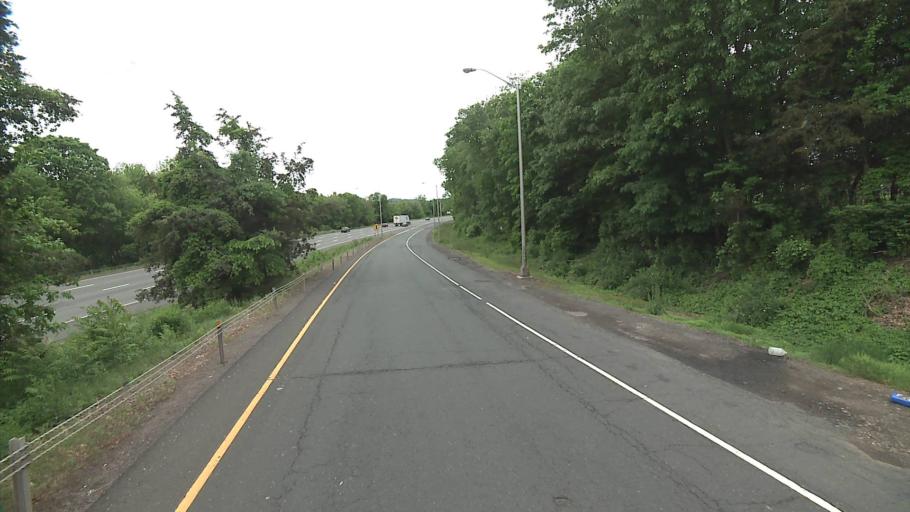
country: US
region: Connecticut
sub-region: Middlesex County
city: Cromwell
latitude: 41.6489
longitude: -72.6736
